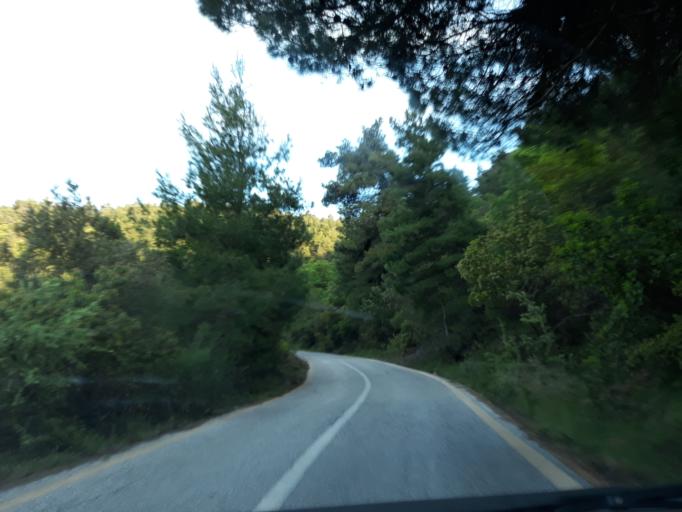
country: GR
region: Attica
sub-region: Nomarchia Anatolikis Attikis
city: Afidnes
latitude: 38.2217
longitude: 23.7816
